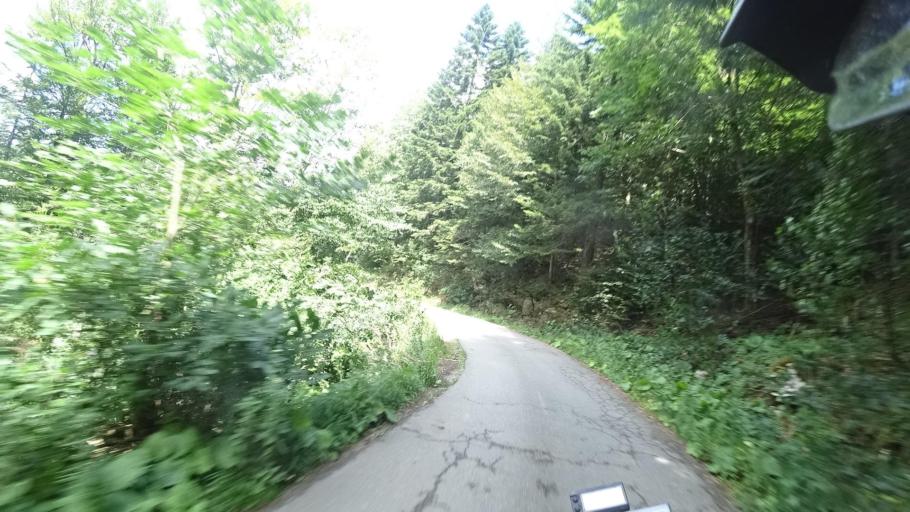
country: HR
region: Licko-Senjska
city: Brinje
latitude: 45.1049
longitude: 15.0136
